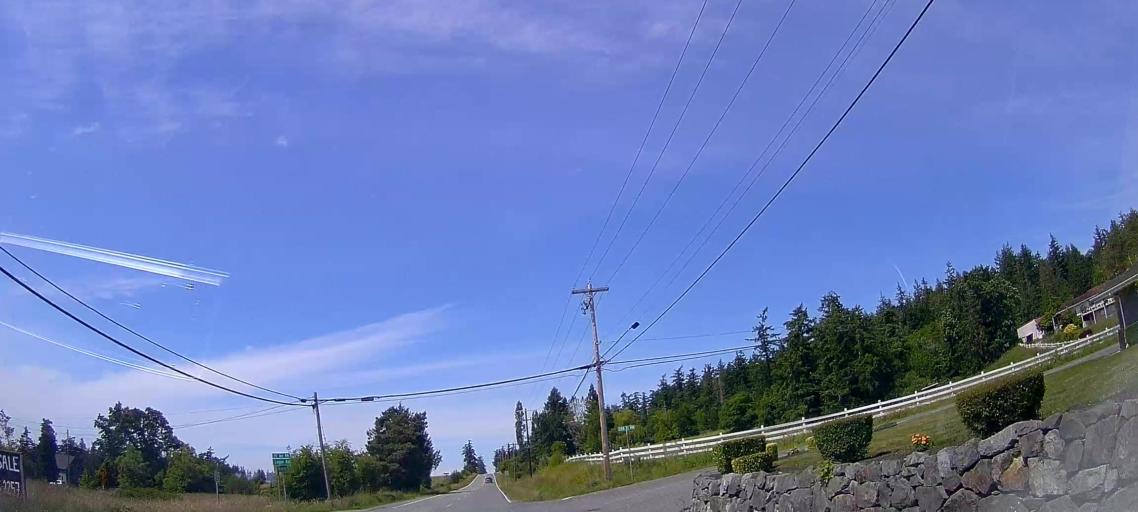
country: US
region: Washington
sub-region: Snohomish County
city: Stanwood
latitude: 48.2575
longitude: -122.3563
